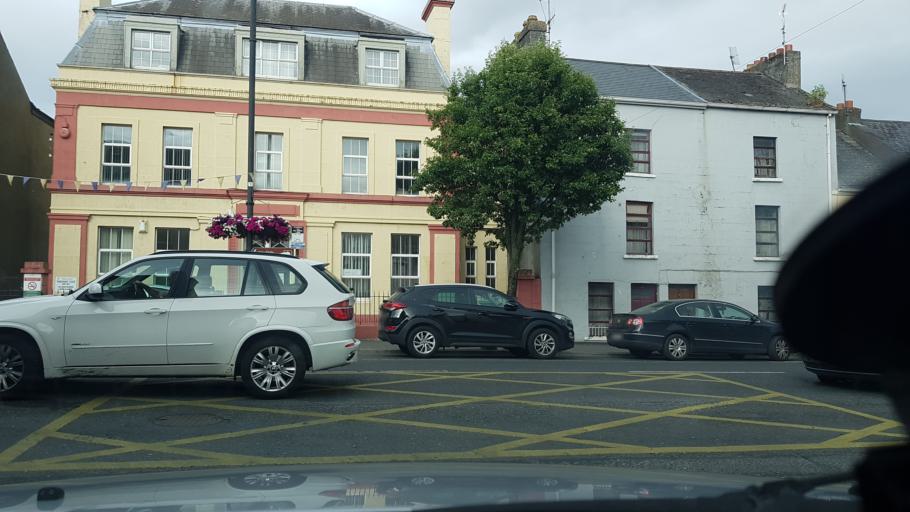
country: IE
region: Munster
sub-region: North Tipperary
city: Nenagh
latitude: 52.8619
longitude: -8.1988
